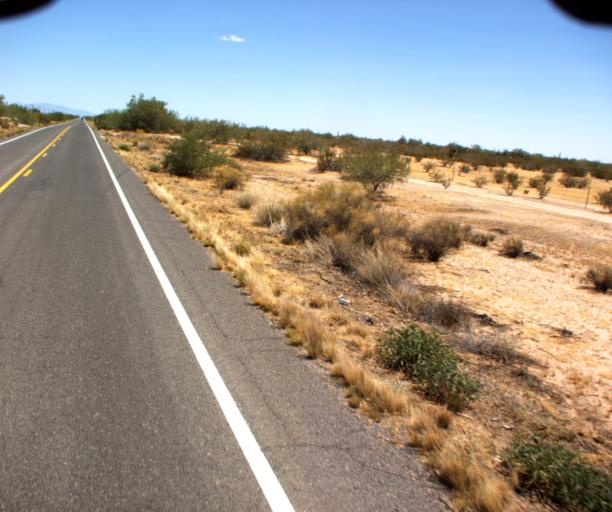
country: US
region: Arizona
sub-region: Pinal County
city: Florence
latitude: 32.9135
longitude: -111.2908
